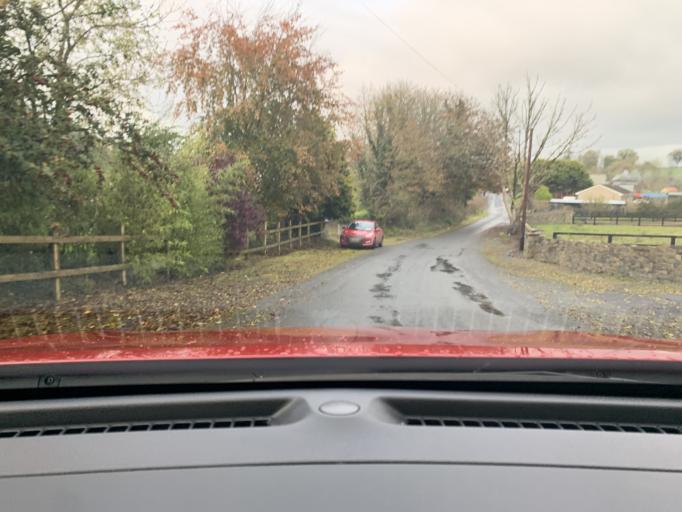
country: IE
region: Connaught
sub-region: Sligo
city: Collooney
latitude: 54.1723
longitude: -8.5116
